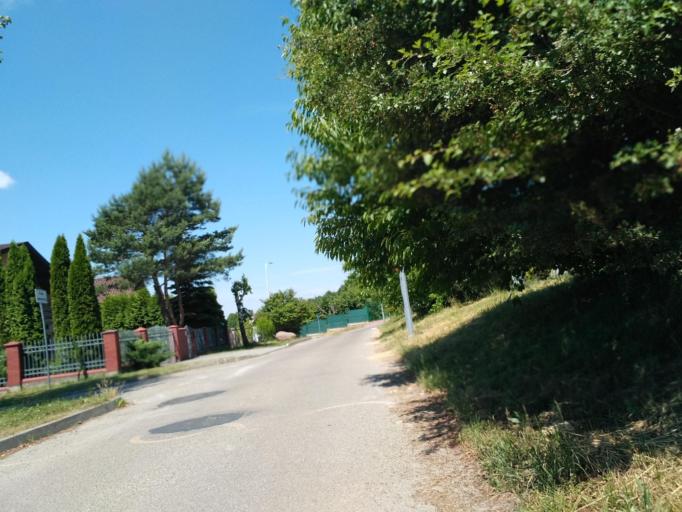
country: PL
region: Subcarpathian Voivodeship
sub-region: Krosno
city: Krosno
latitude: 49.7050
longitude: 21.7701
